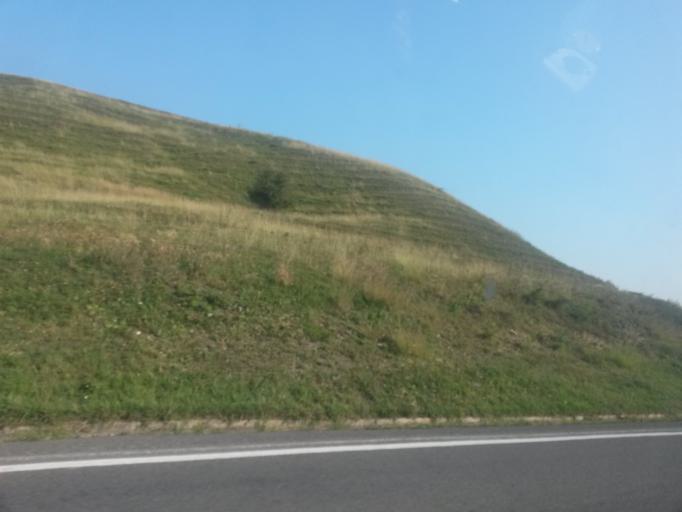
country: RO
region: Alba
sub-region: Comuna Unirea
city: Unirea
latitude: 46.4250
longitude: 23.8014
